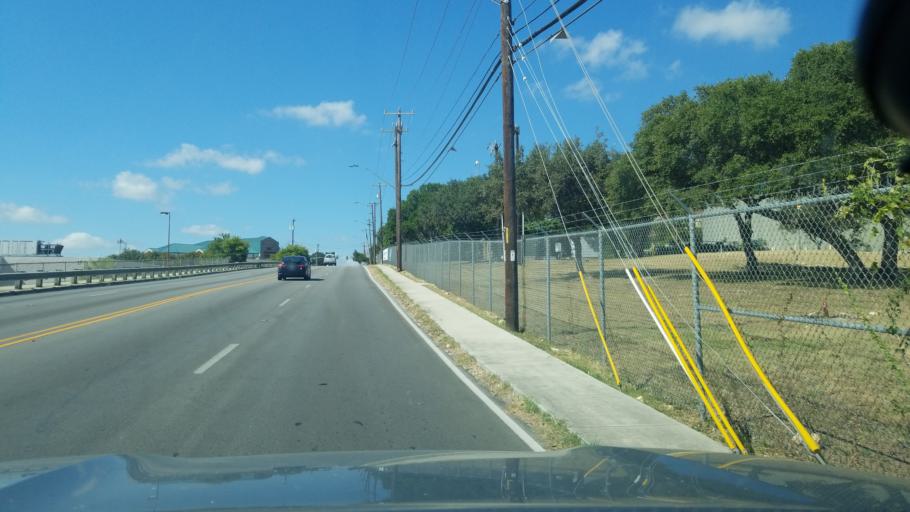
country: US
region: Texas
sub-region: Bexar County
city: Hollywood Park
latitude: 29.5675
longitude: -98.4875
